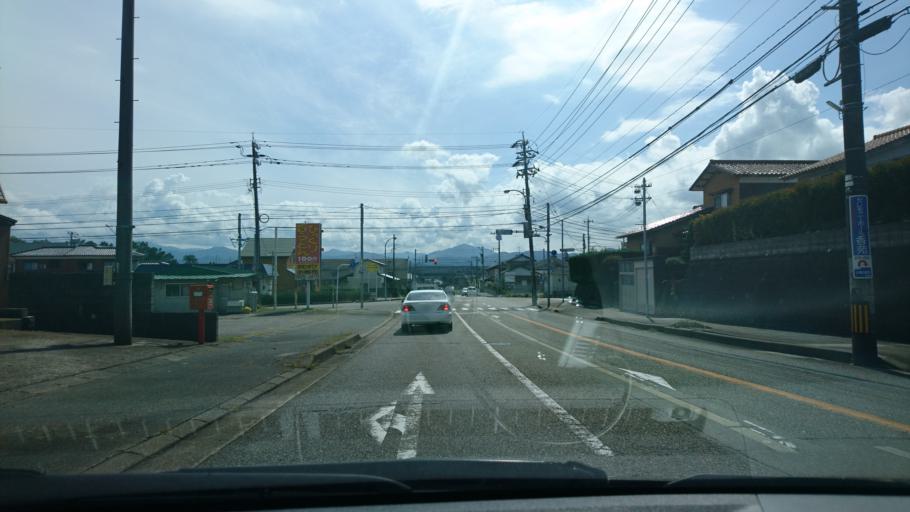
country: JP
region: Ishikawa
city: Komatsu
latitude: 36.3257
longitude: 136.3575
